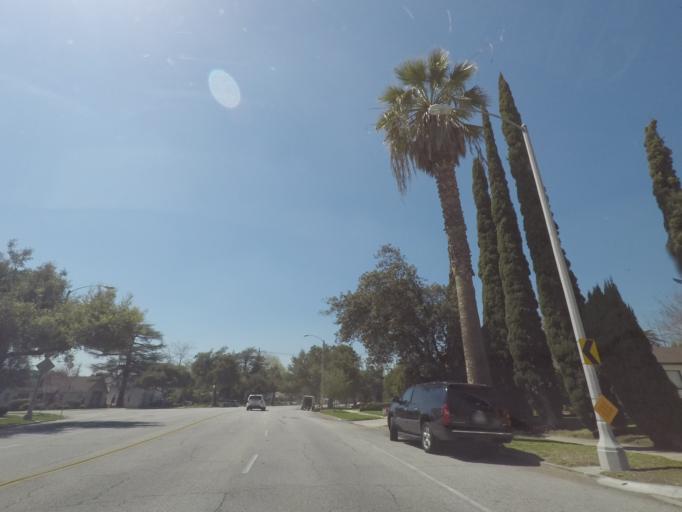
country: US
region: California
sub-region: Los Angeles County
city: East Pasadena
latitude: 34.1582
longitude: -118.1076
